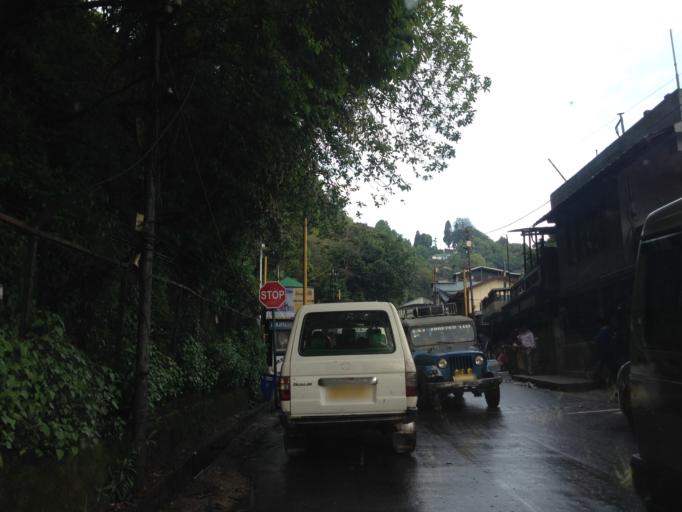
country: IN
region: West Bengal
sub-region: Darjiling
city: Darjiling
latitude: 27.0560
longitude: 88.2548
